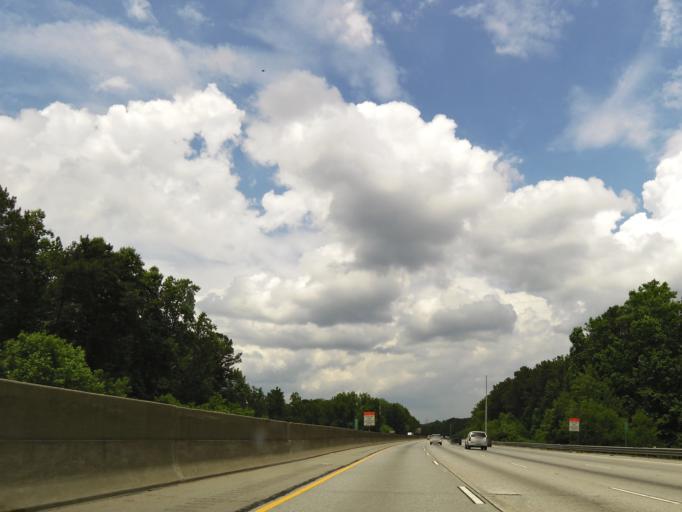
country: US
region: Georgia
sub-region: Fulton County
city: East Point
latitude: 33.6961
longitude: -84.4998
